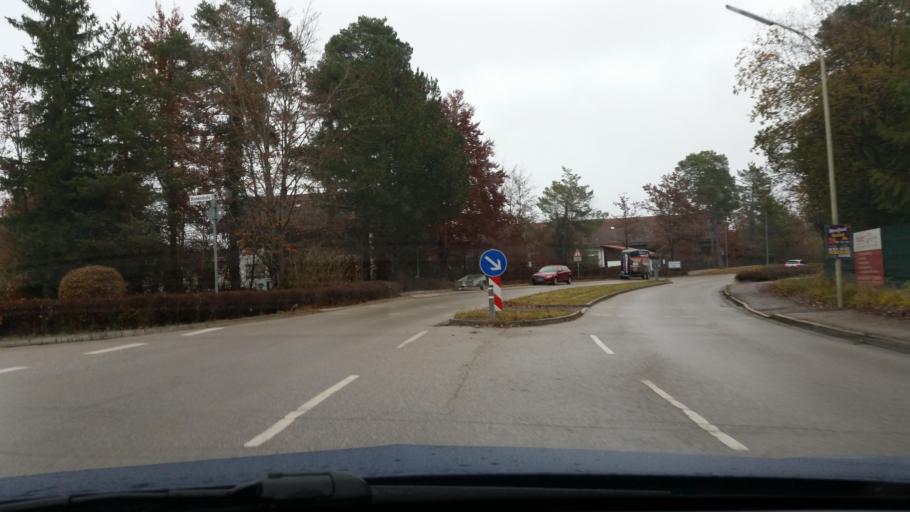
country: DE
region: Bavaria
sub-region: Upper Bavaria
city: Geretsried
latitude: 47.8845
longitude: 11.4617
